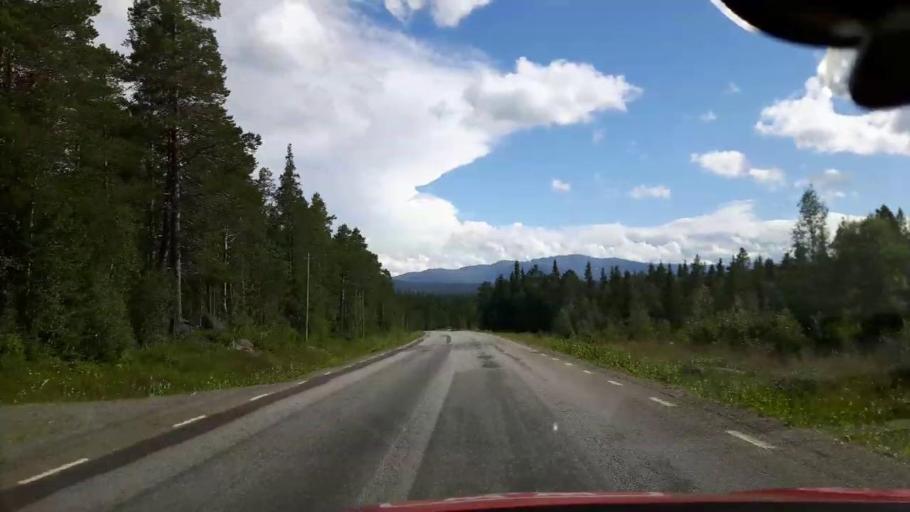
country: SE
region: Jaemtland
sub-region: Are Kommun
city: Are
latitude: 63.2253
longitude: 13.1610
